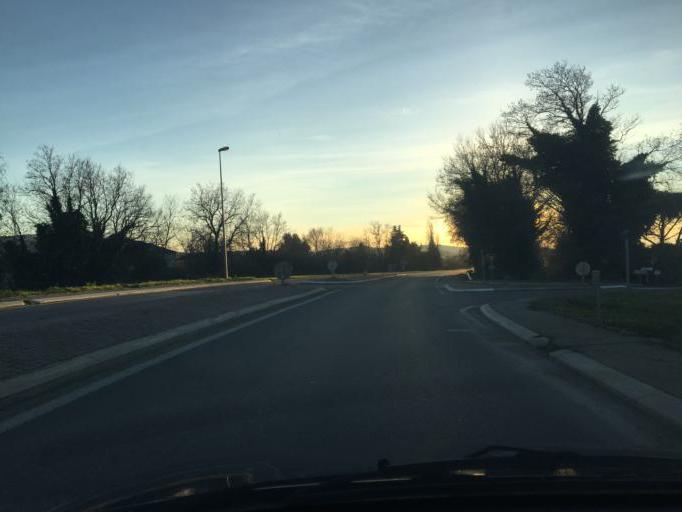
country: FR
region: Provence-Alpes-Cote d'Azur
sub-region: Departement des Bouches-du-Rhone
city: Mallemort
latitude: 43.7337
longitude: 5.1713
